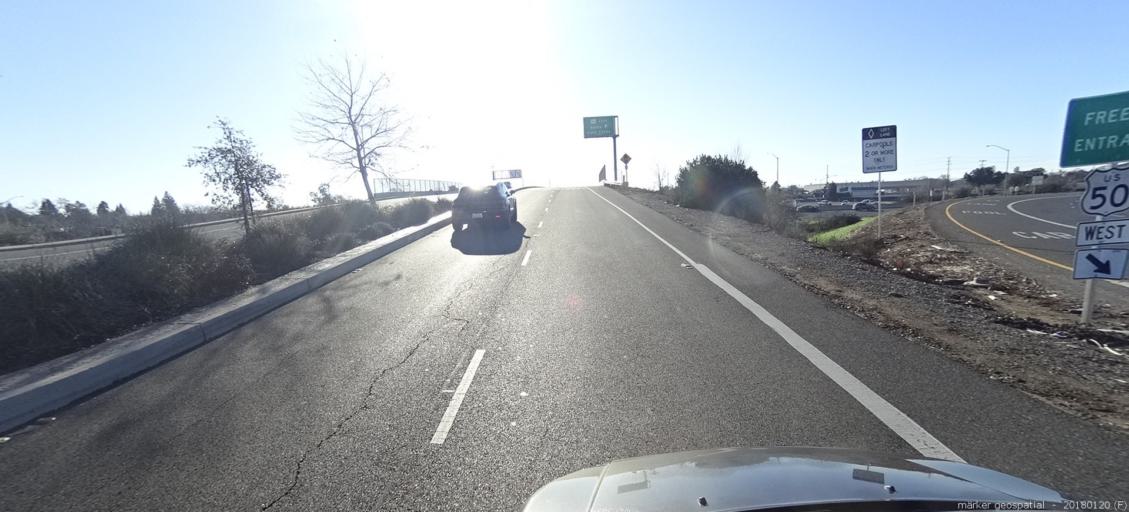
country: US
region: California
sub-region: Sacramento County
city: Gold River
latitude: 38.6318
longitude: -121.2180
